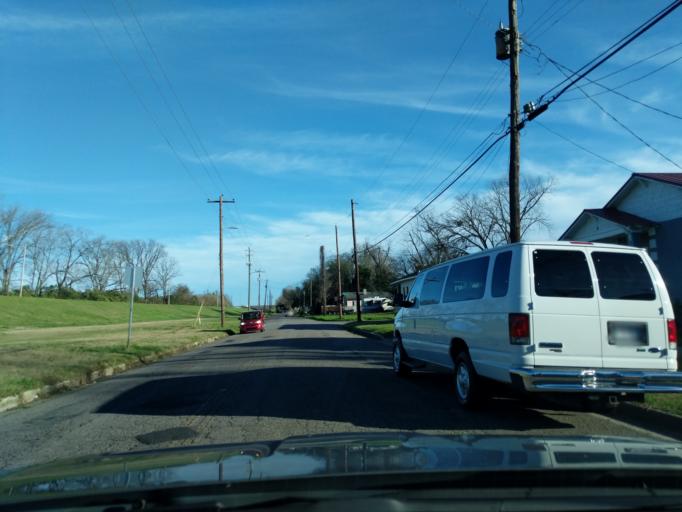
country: US
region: Georgia
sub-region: Richmond County
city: Augusta
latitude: 33.4716
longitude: -81.9515
